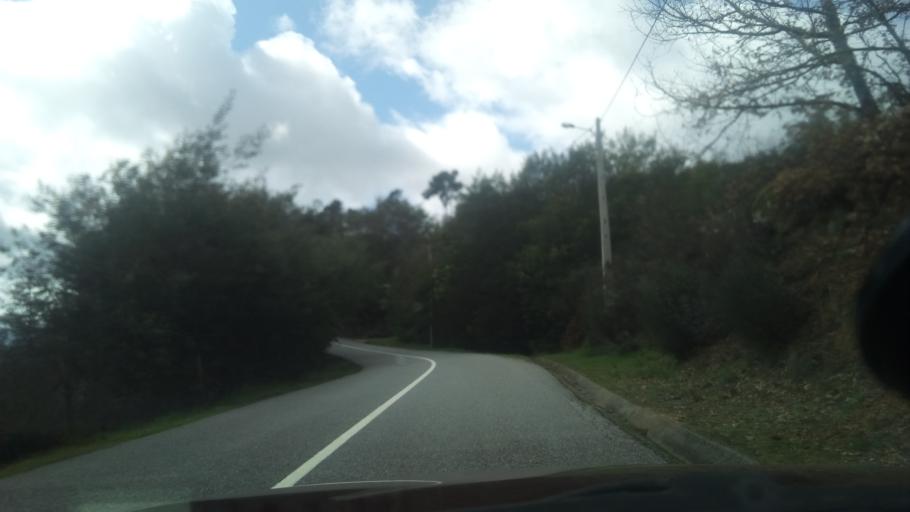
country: PT
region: Guarda
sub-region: Fornos de Algodres
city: Fornos de Algodres
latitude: 40.6185
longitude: -7.4814
